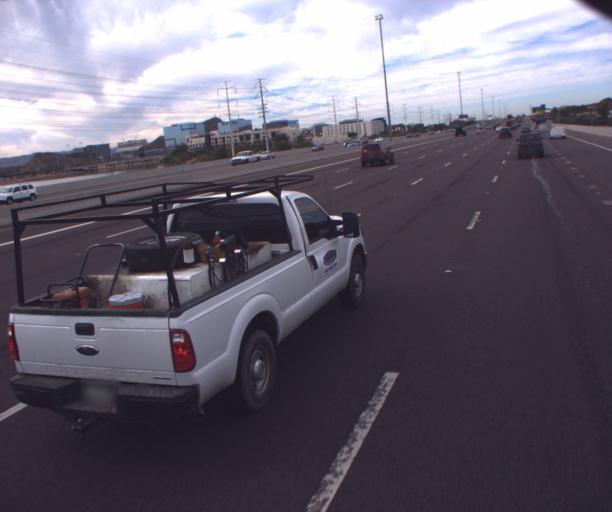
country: US
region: Arizona
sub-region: Maricopa County
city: Tempe
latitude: 33.4363
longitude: -111.9173
